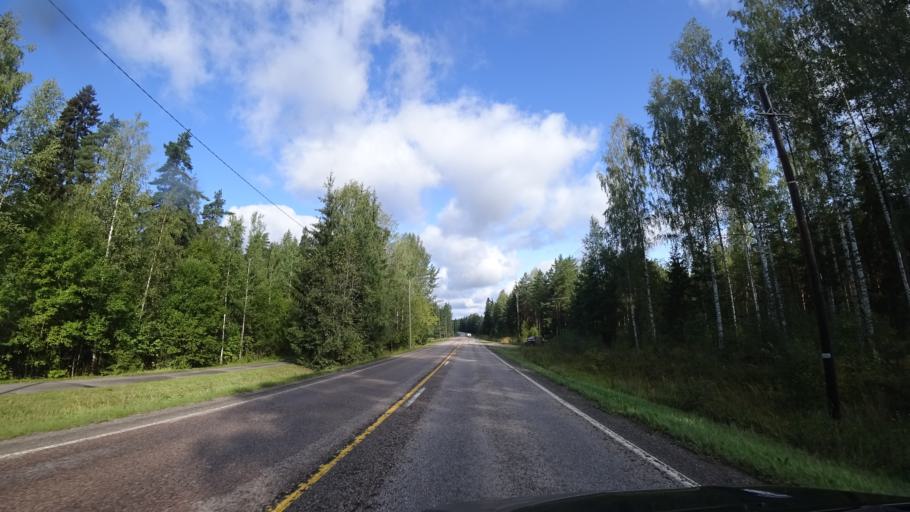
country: FI
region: Uusimaa
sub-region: Helsinki
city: Tuusula
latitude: 60.4252
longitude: 24.9972
